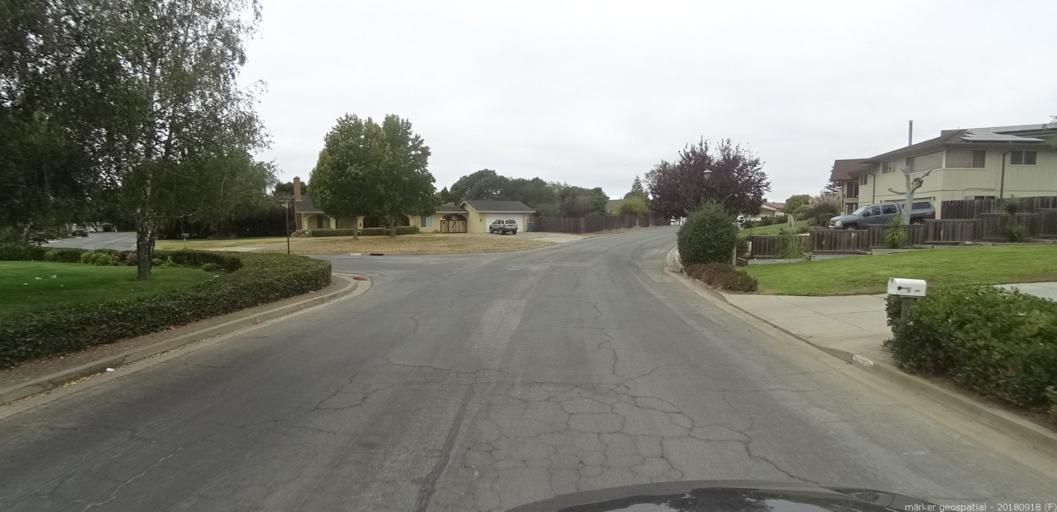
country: US
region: California
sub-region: Monterey County
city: Prunedale
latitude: 36.7455
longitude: -121.6290
